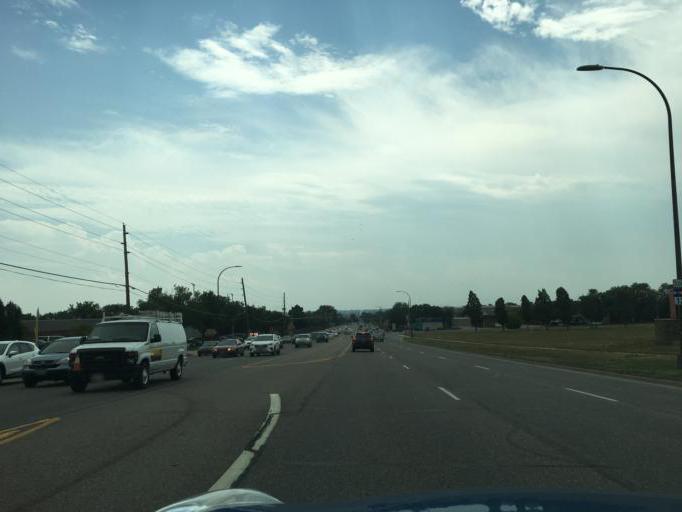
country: US
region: Colorado
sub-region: Jefferson County
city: Arvada
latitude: 39.8224
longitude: -105.0815
